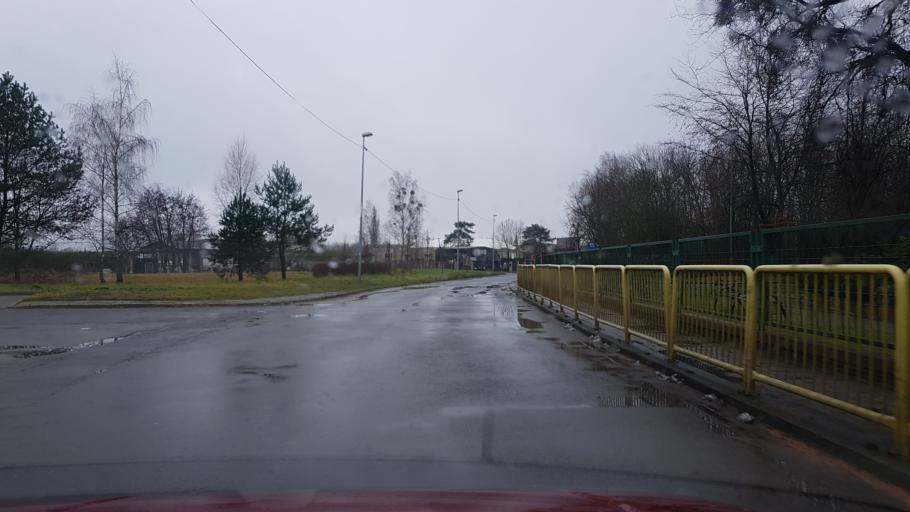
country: PL
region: West Pomeranian Voivodeship
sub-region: Powiat policki
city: Police
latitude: 53.5519
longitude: 14.5418
